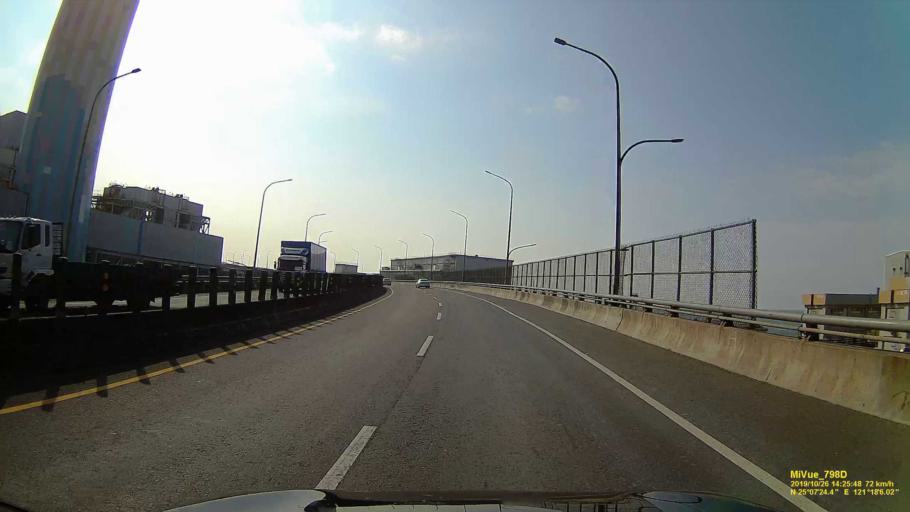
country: TW
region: Taiwan
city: Taoyuan City
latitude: 25.1233
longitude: 121.3026
